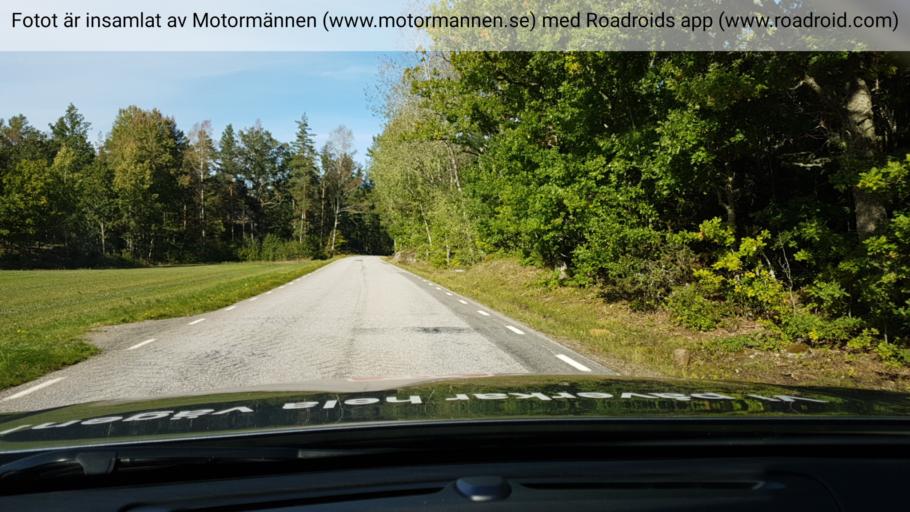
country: SE
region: OEstergoetland
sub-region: Valdemarsviks Kommun
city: Valdemarsvik
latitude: 58.0872
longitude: 16.6391
